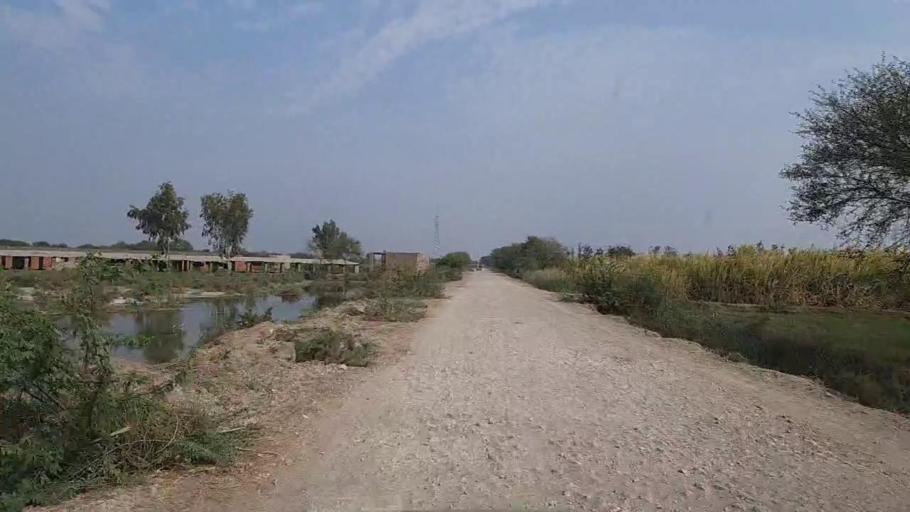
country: PK
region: Sindh
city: Mirwah Gorchani
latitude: 25.3728
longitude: 69.0332
